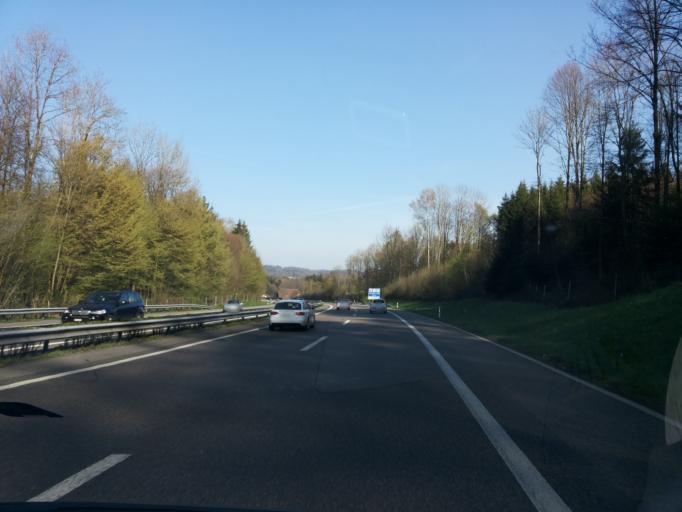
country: CH
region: Aargau
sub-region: Bezirk Zofingen
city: Uerkheim
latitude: 47.3219
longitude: 8.0107
